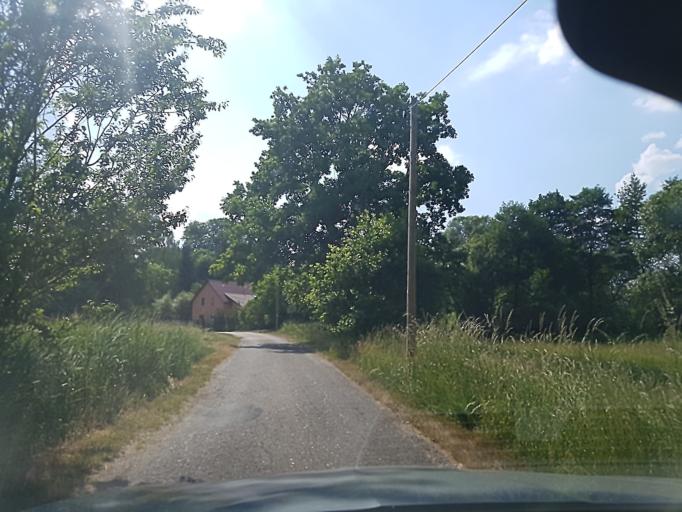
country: DE
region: Brandenburg
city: Ruckersdorf
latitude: 51.5553
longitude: 13.5556
